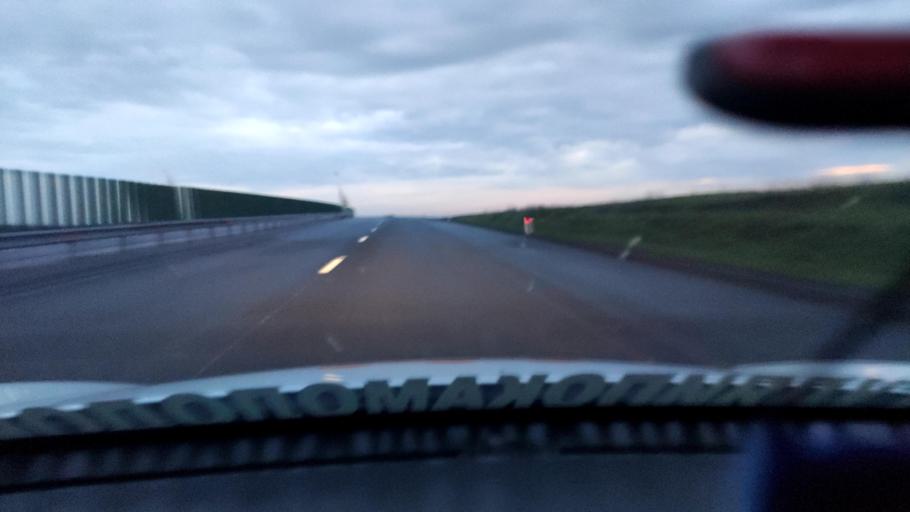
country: RU
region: Rostov
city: Tarasovskiy
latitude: 48.7383
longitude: 40.3999
